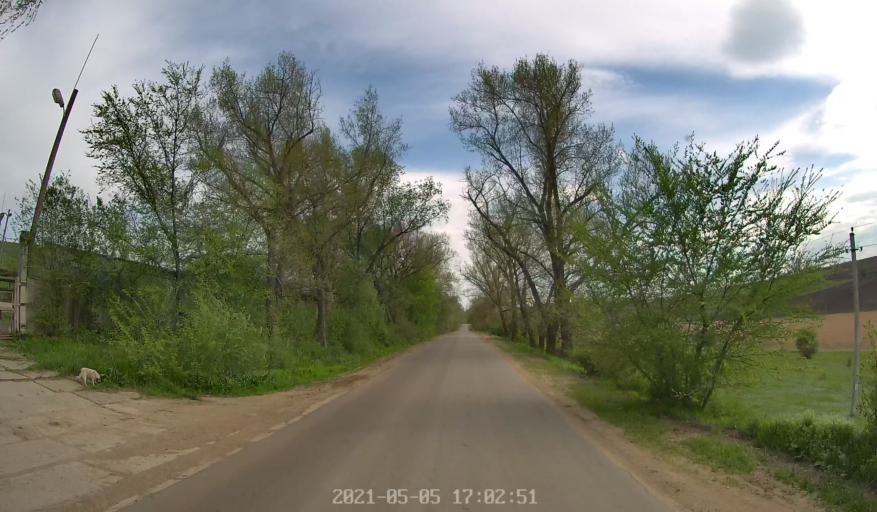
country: MD
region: Chisinau
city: Vadul lui Voda
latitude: 47.0567
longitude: 29.1323
